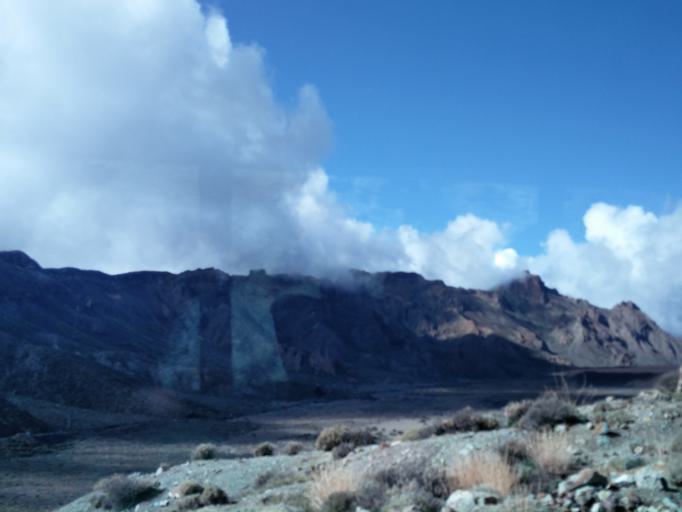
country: ES
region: Canary Islands
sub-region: Provincia de Santa Cruz de Tenerife
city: Vilaflor
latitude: 28.2178
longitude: -16.6271
